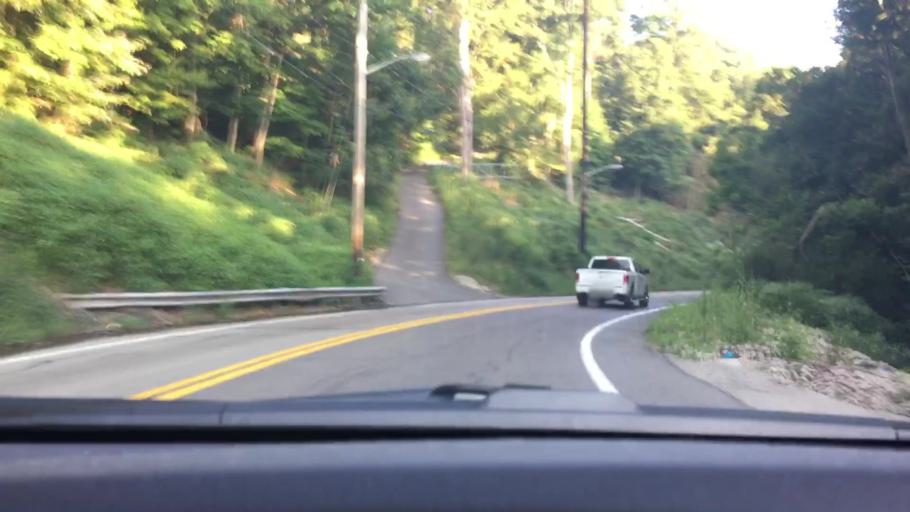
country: US
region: Pennsylvania
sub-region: Allegheny County
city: West Homestead
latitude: 40.3740
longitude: -79.9201
